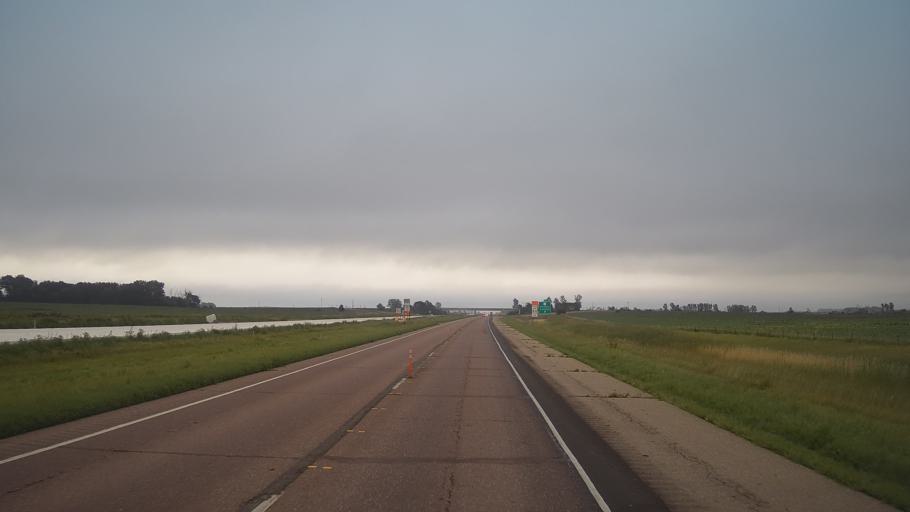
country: US
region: Minnesota
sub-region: Faribault County
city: Winnebago
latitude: 43.6662
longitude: -94.2374
